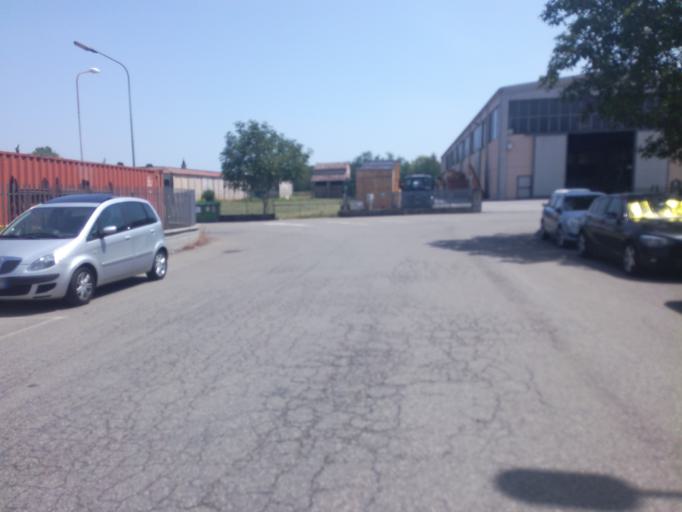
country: IT
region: Emilia-Romagna
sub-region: Provincia di Parma
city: Soragna
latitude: 44.9226
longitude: 10.1167
